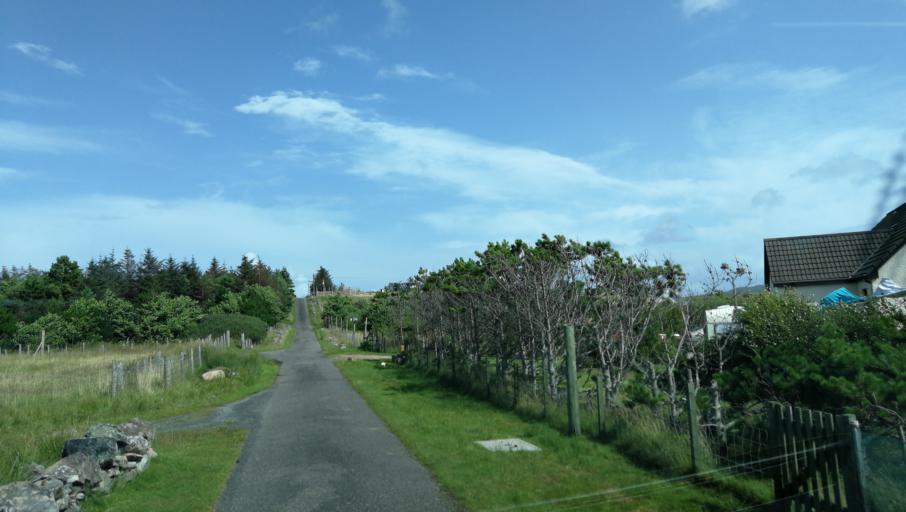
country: GB
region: Scotland
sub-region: Highland
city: Portree
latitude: 57.7434
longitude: -5.7767
